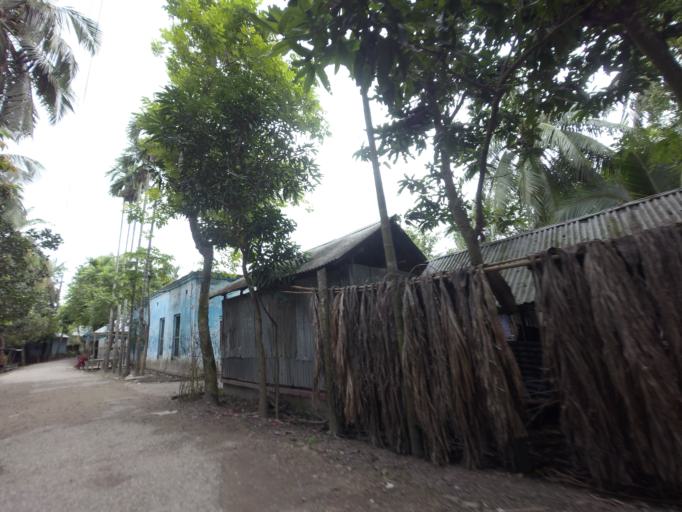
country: BD
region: Khulna
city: Kalia
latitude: 23.0492
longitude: 89.6460
